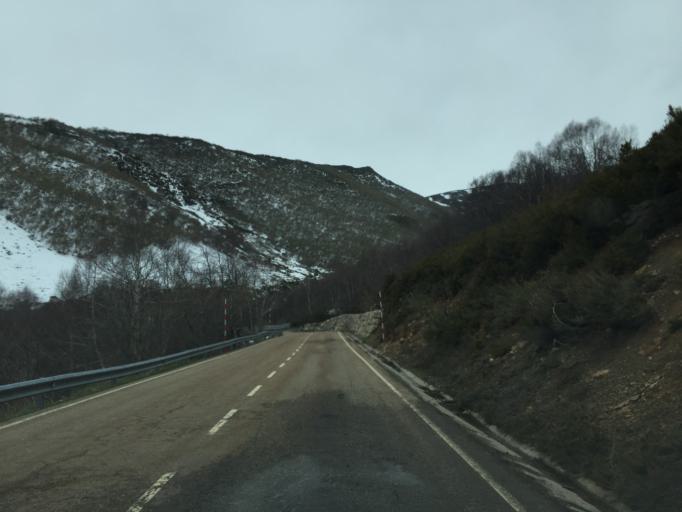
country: ES
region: Castille and Leon
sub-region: Provincia de Leon
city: San Emiliano
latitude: 43.0497
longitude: -6.0218
